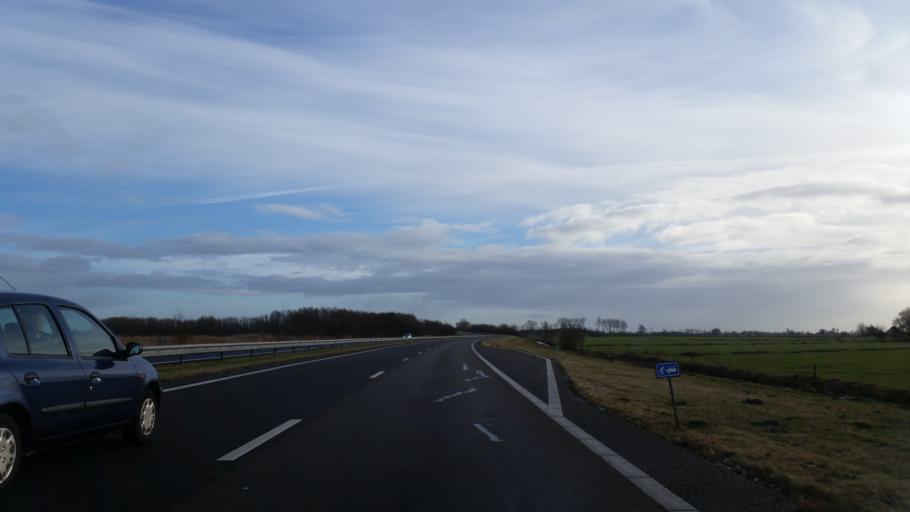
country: NL
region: Friesland
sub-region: Gemeente Boarnsterhim
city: Warten
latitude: 53.1675
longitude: 5.9134
